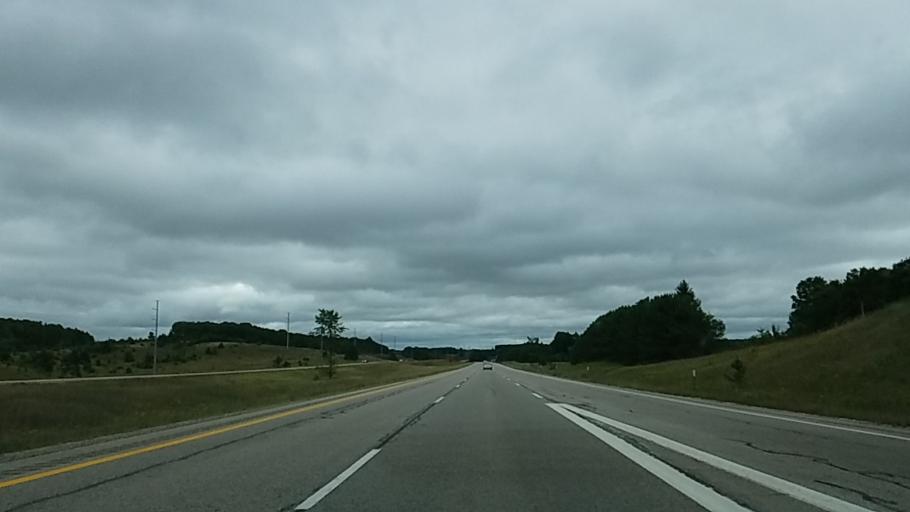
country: US
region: Michigan
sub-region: Otsego County
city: Gaylord
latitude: 45.1052
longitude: -84.6884
